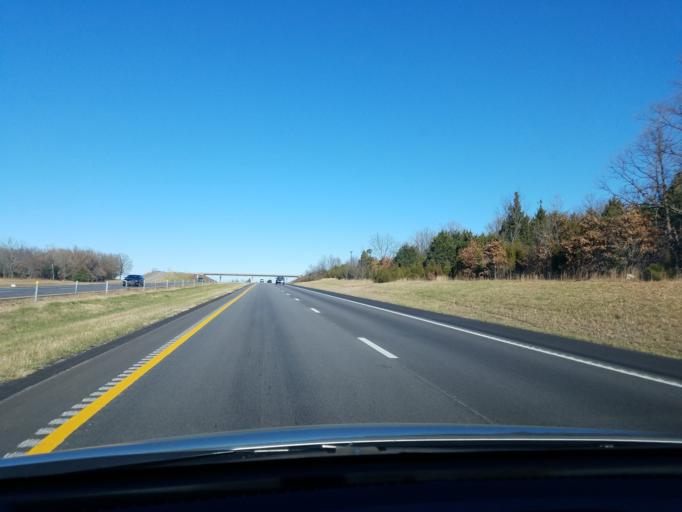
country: US
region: Missouri
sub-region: Webster County
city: Marshfield
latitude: 37.3797
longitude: -92.9036
